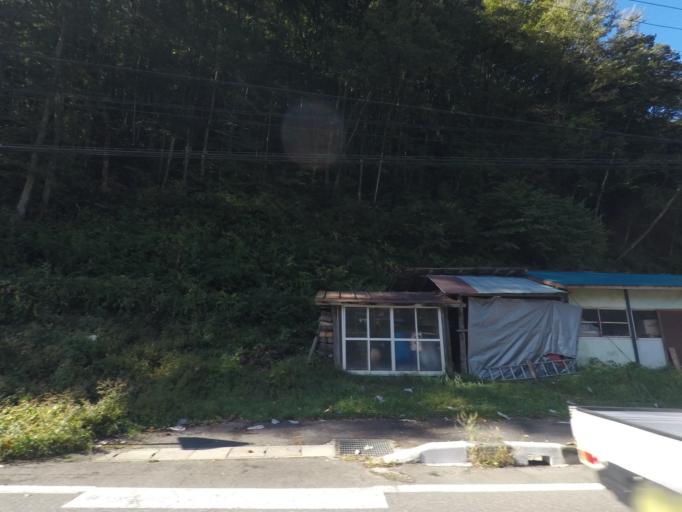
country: JP
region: Nagano
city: Tatsuno
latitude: 35.9668
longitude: 137.7645
